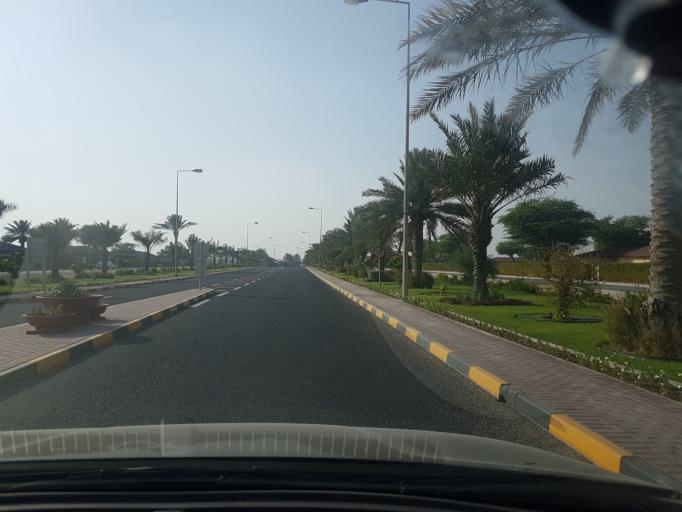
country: BH
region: Northern
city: Ar Rifa'
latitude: 26.0946
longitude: 50.5466
